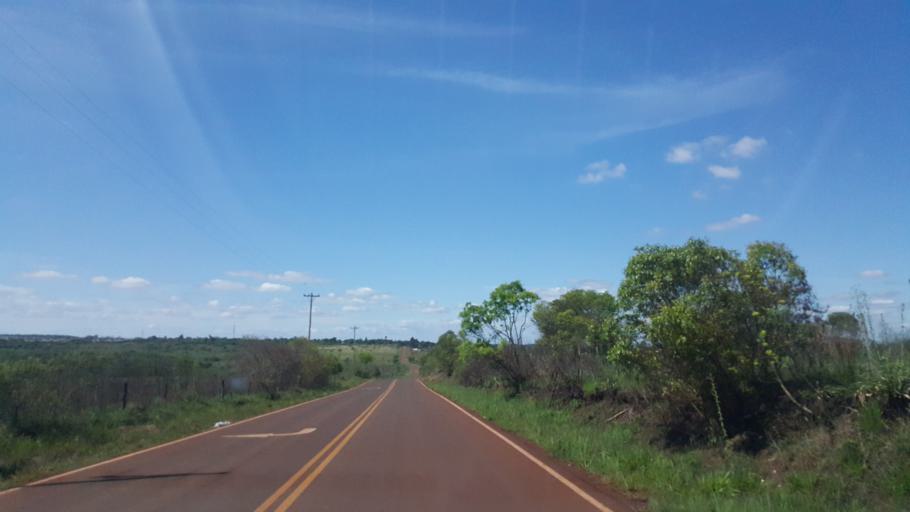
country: AR
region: Misiones
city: Garupa
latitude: -27.4970
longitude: -55.8419
